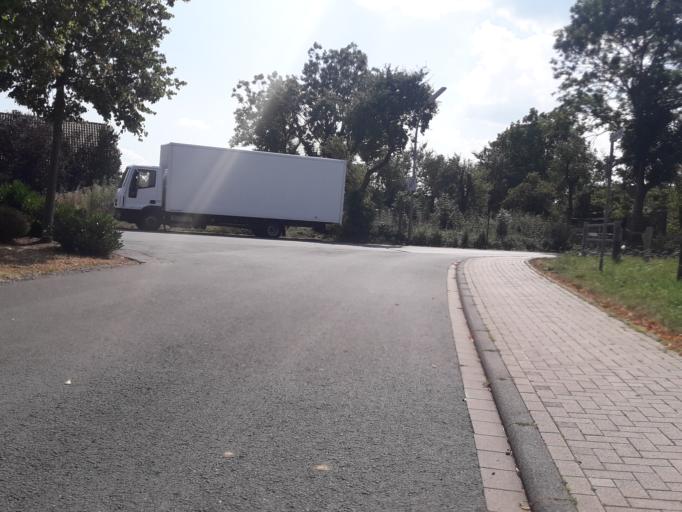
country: DE
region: North Rhine-Westphalia
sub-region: Regierungsbezirk Detmold
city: Salzkotten
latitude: 51.6095
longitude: 8.6550
